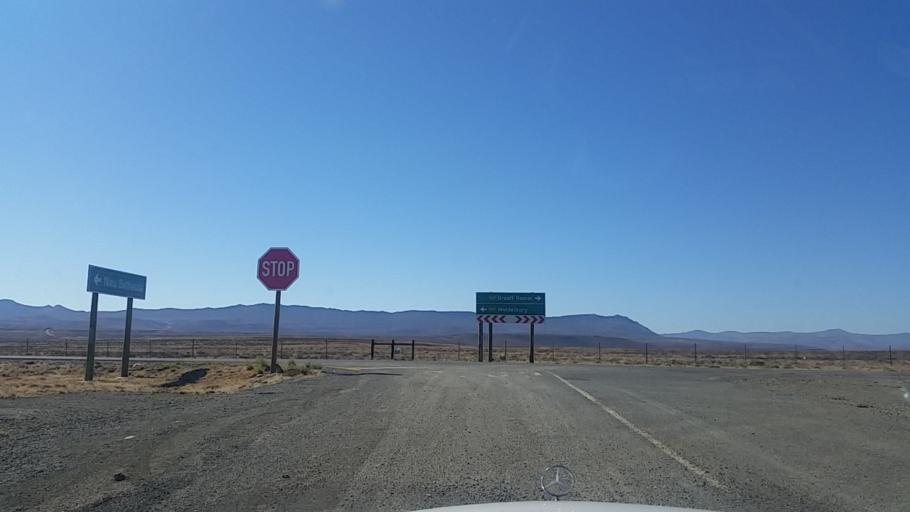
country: ZA
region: Eastern Cape
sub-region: Cacadu District Municipality
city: Graaff-Reinet
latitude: -31.9103
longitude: 24.7643
